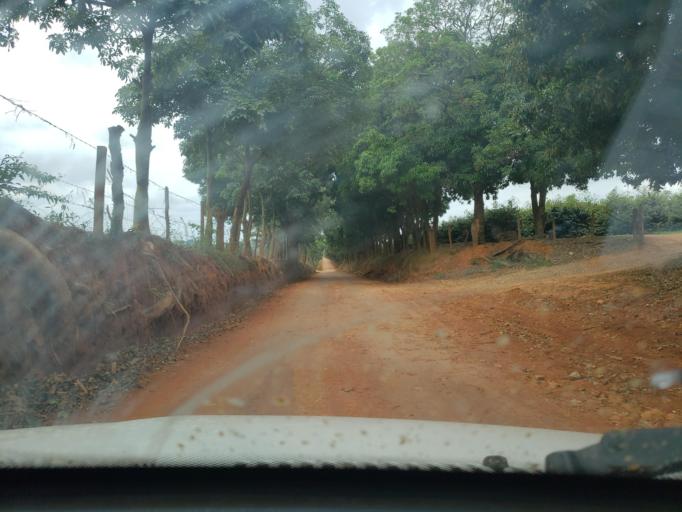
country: BR
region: Minas Gerais
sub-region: Boa Esperanca
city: Boa Esperanca
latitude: -20.9890
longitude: -45.5958
